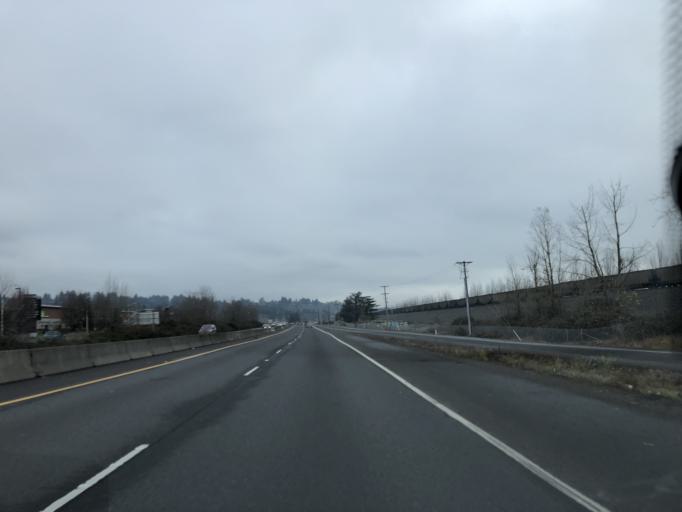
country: US
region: Washington
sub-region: Clark County
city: Vancouver
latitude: 45.6183
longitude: -122.6478
